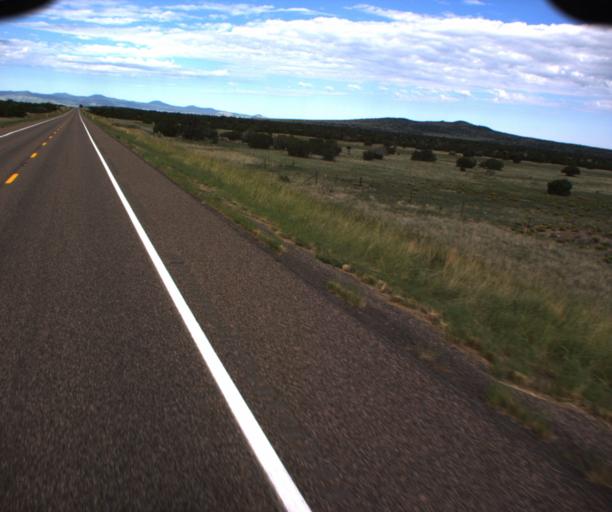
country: US
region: Arizona
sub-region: Apache County
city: Springerville
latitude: 34.1491
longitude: -109.1827
